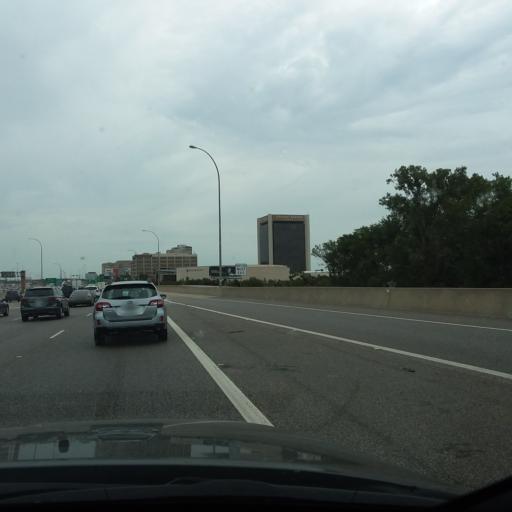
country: US
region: Texas
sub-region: Dallas County
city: Richardson
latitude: 32.9241
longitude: -96.7829
